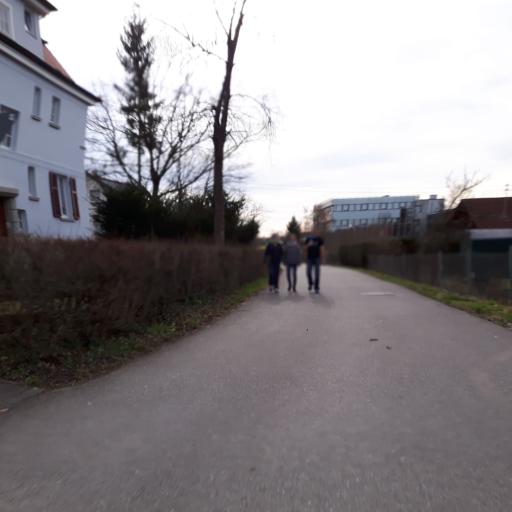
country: DE
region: Baden-Wuerttemberg
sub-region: Regierungsbezirk Stuttgart
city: Grossbottwar
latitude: 48.9981
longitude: 9.2943
